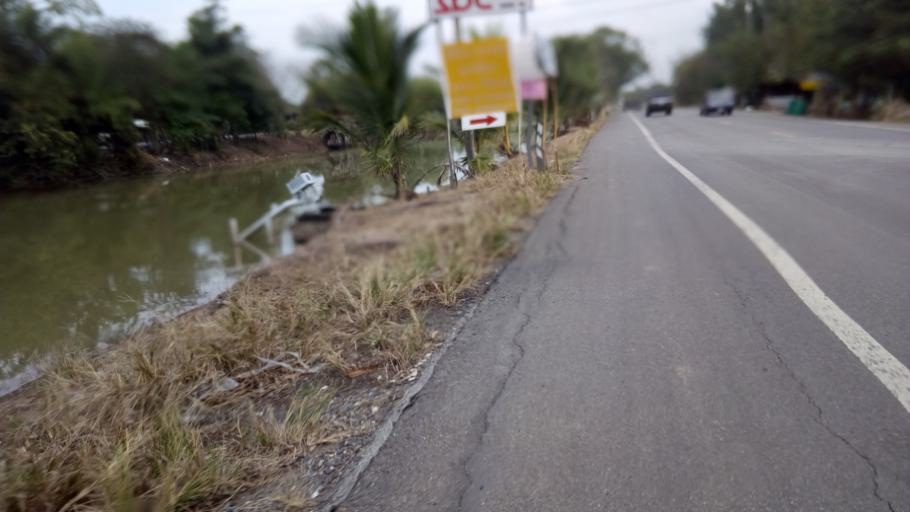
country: TH
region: Pathum Thani
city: Nong Suea
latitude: 14.2136
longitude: 100.8234
